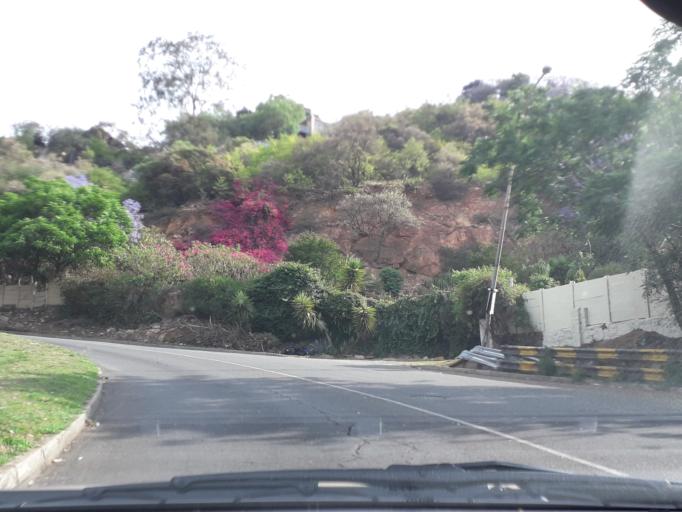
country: ZA
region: Gauteng
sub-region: City of Johannesburg Metropolitan Municipality
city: Johannesburg
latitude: -26.1676
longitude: 28.0874
